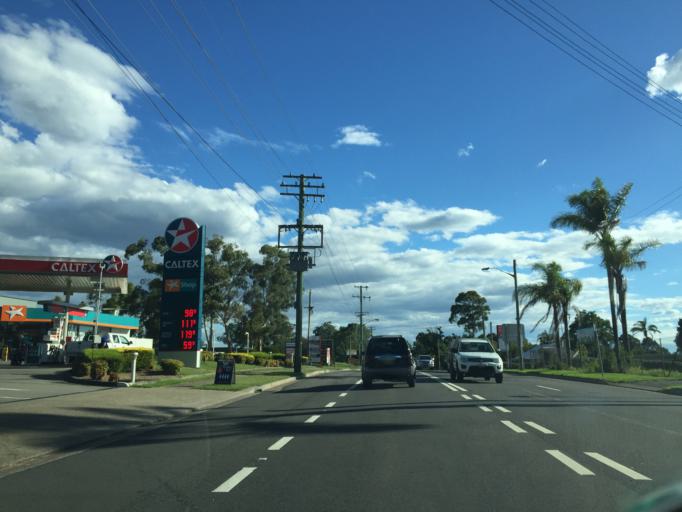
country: AU
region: New South Wales
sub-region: The Hills Shire
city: Glenhaven
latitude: -33.6825
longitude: 151.0283
